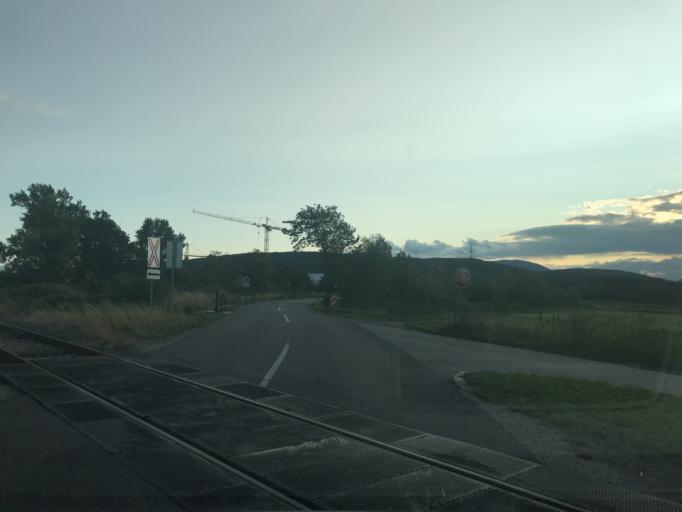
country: AT
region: Lower Austria
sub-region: Politischer Bezirk Wiener Neustadt
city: Theresienfeld
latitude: 47.8655
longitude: 16.1981
